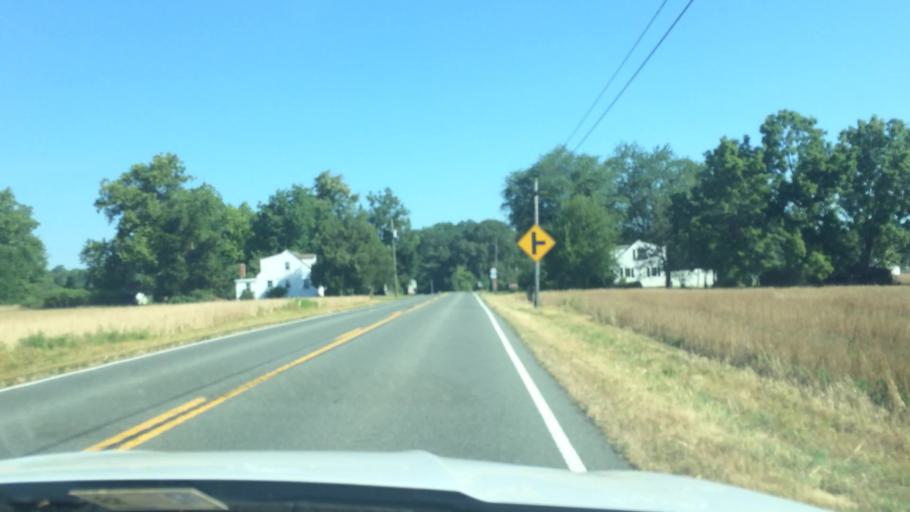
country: US
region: Virginia
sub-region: Northumberland County
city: Heathsville
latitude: 37.8450
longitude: -76.5804
